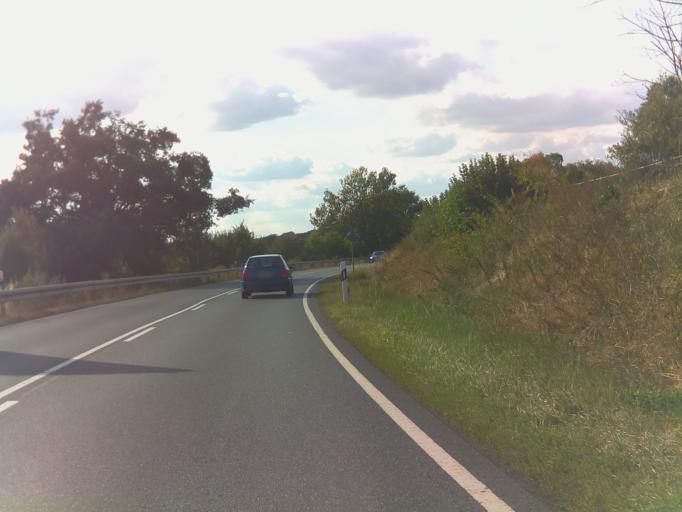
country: DE
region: Hesse
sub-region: Regierungsbezirk Kassel
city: Dipperz
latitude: 50.5285
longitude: 9.8265
